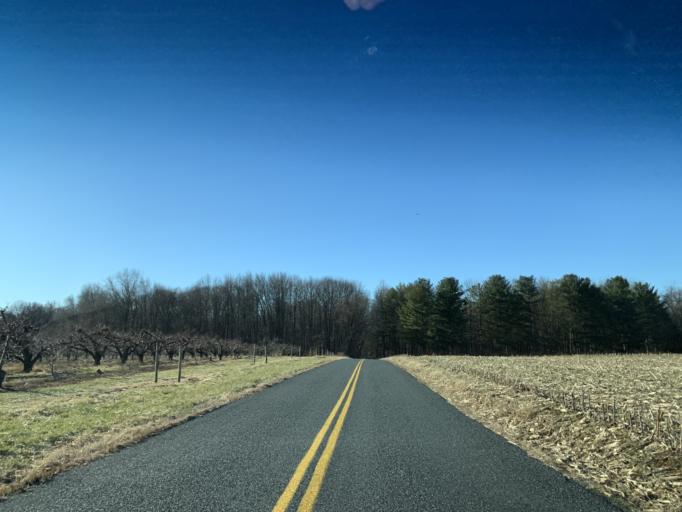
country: US
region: Maryland
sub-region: Harford County
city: Riverside
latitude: 39.5426
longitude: -76.2391
